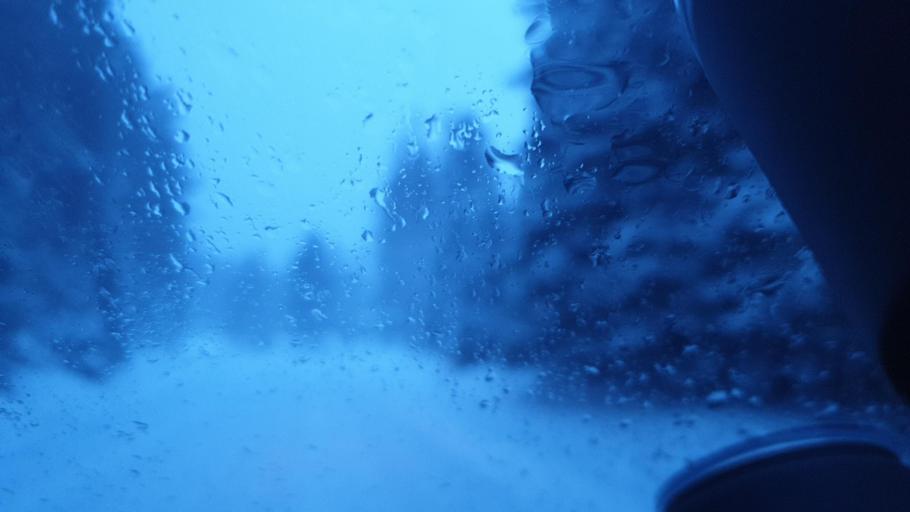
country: SE
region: Vaermland
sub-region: Eda Kommun
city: Charlottenberg
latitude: 59.8951
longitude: 12.3001
